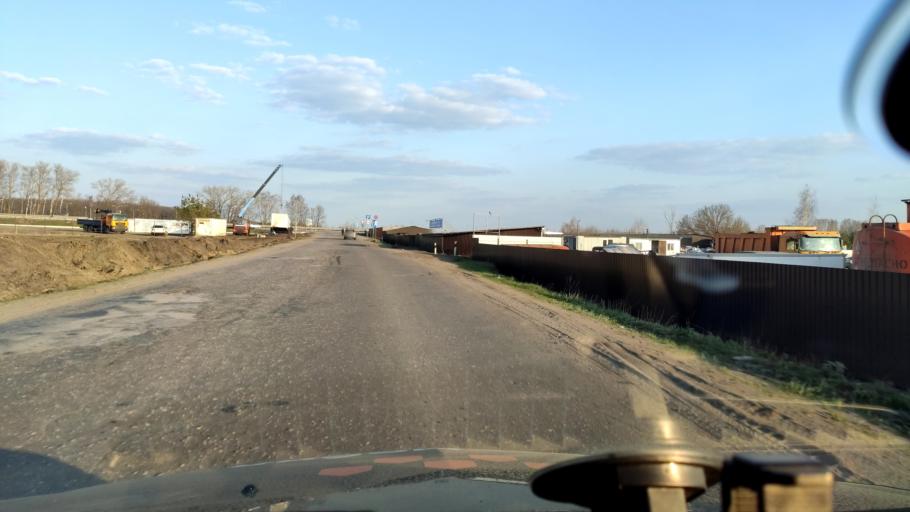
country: RU
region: Voronezj
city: Podgornoye
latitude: 51.8280
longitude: 39.2083
